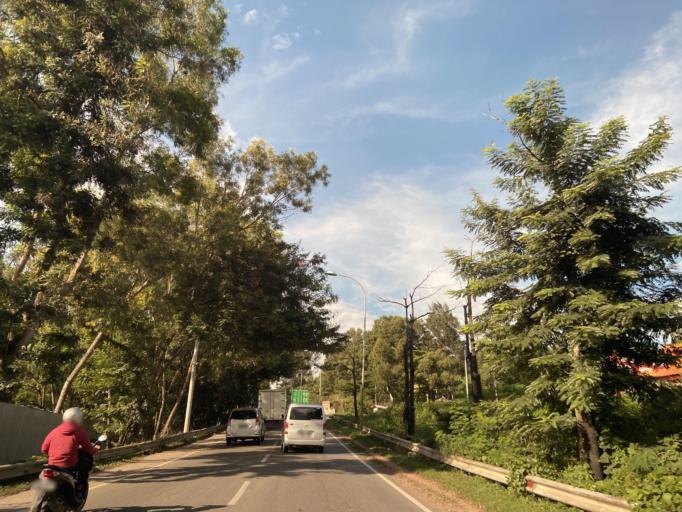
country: SG
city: Singapore
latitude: 1.1211
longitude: 104.0060
